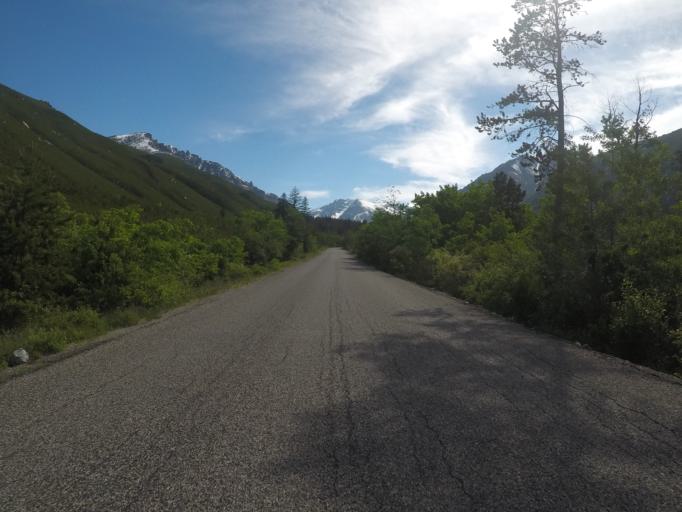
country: US
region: Montana
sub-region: Stillwater County
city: Absarokee
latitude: 45.2480
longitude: -109.5759
